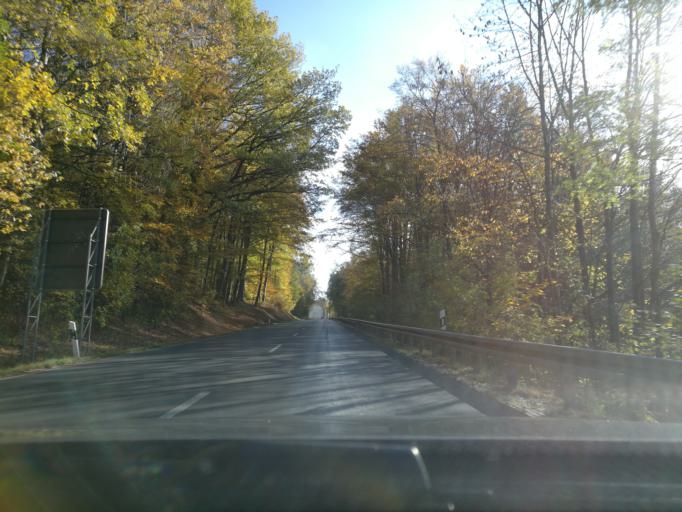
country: DE
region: Hesse
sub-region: Regierungsbezirk Kassel
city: Gersfeld
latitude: 50.4372
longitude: 9.9187
